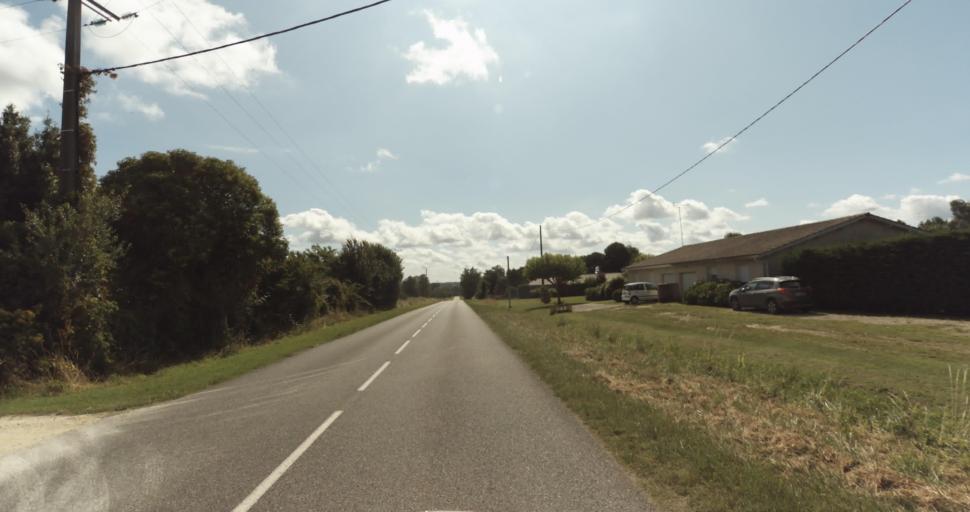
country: FR
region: Aquitaine
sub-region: Departement de la Gironde
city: Bazas
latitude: 44.4409
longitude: -0.1917
